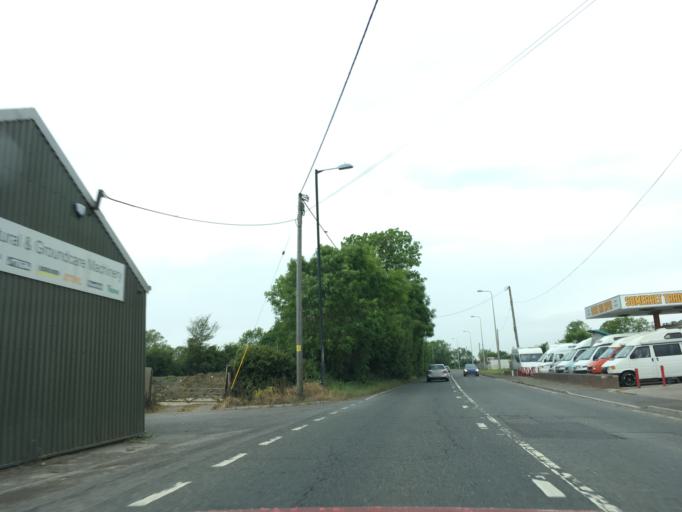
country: GB
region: England
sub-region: North Somerset
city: Kingston Seymour
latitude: 51.3756
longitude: -2.8555
